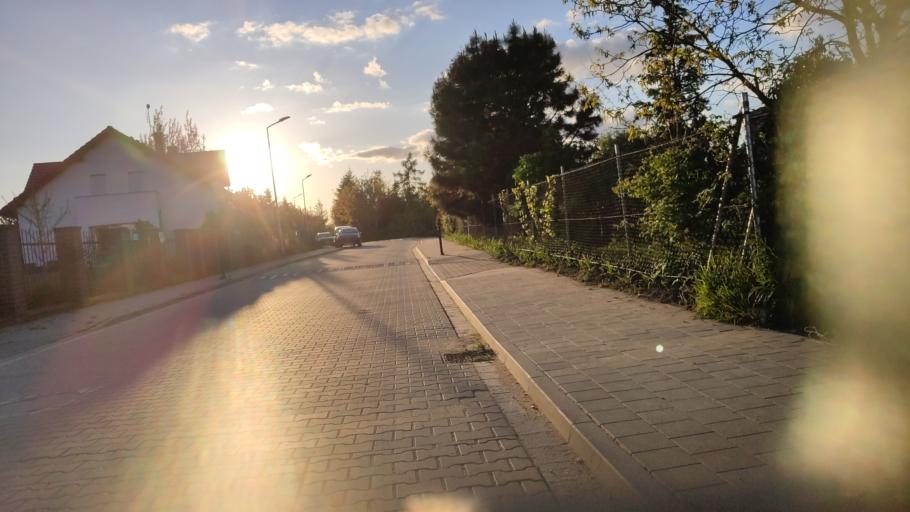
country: PL
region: Lower Silesian Voivodeship
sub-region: Powiat wroclawski
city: Zerniki Wroclawskie
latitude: 51.0536
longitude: 17.0353
